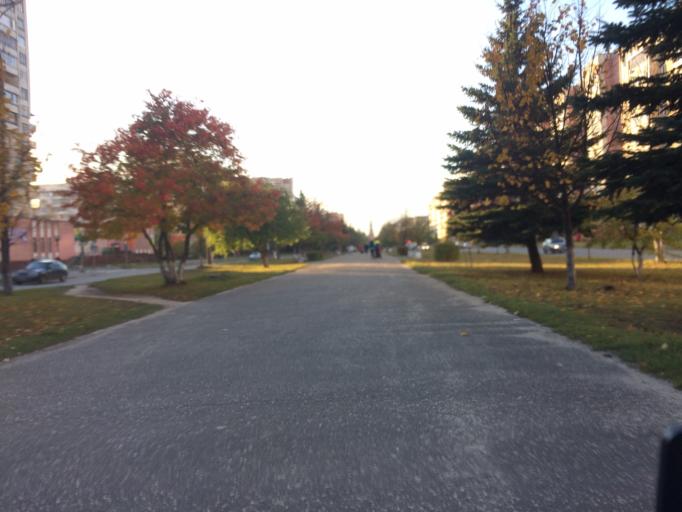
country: RU
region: Mariy-El
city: Yoshkar-Ola
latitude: 56.6292
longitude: 47.9246
